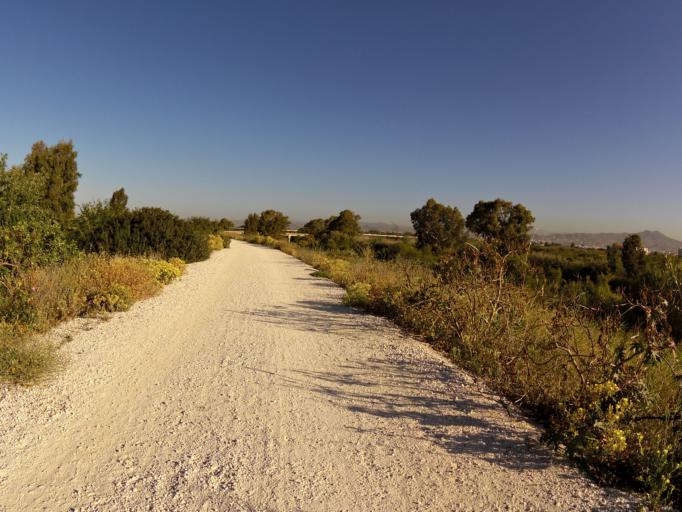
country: ES
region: Andalusia
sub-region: Provincia de Malaga
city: Malaga
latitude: 36.6705
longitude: -4.4603
